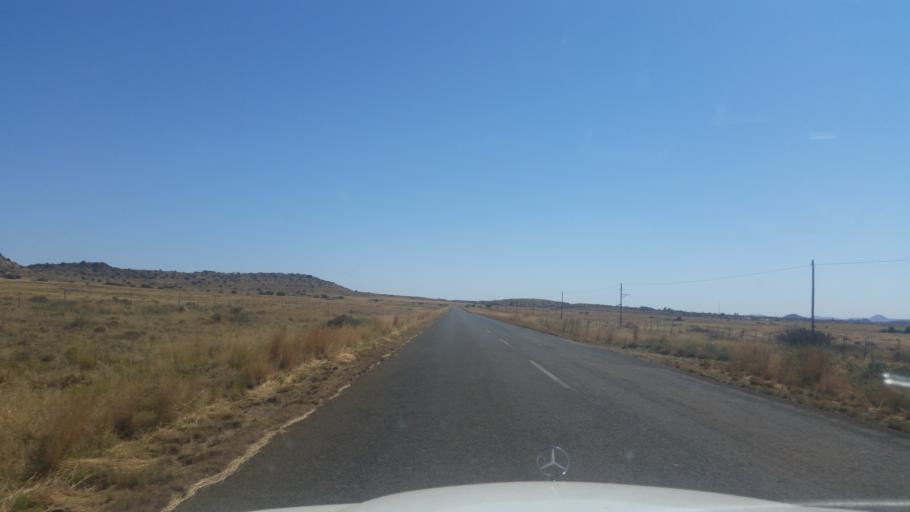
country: ZA
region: Eastern Cape
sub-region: Joe Gqabi District Municipality
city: Burgersdorp
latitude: -30.7254
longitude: 25.7550
